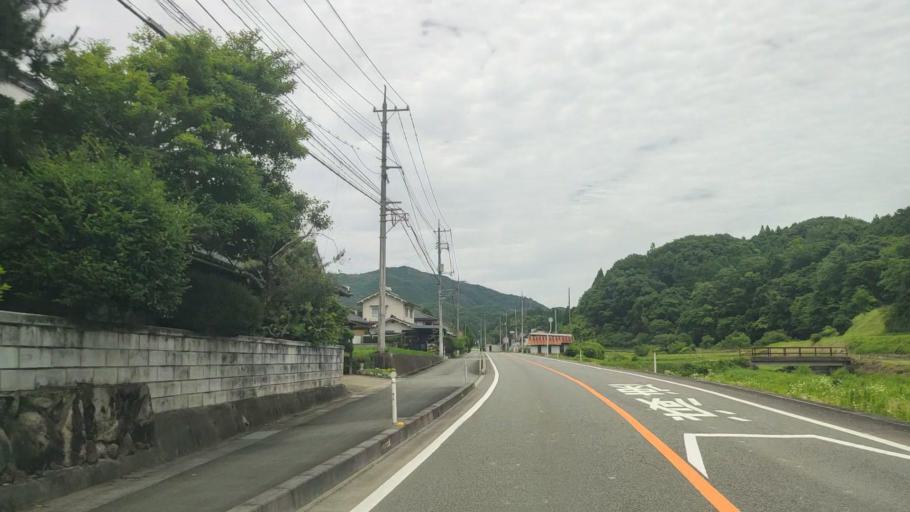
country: JP
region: Okayama
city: Tsuyama
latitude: 35.0769
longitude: 134.2458
